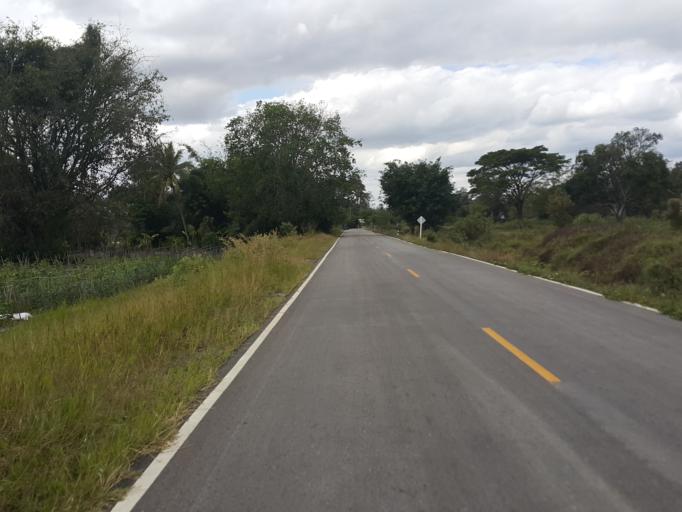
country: TH
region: Chiang Mai
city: San Kamphaeng
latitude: 18.8384
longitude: 99.1578
